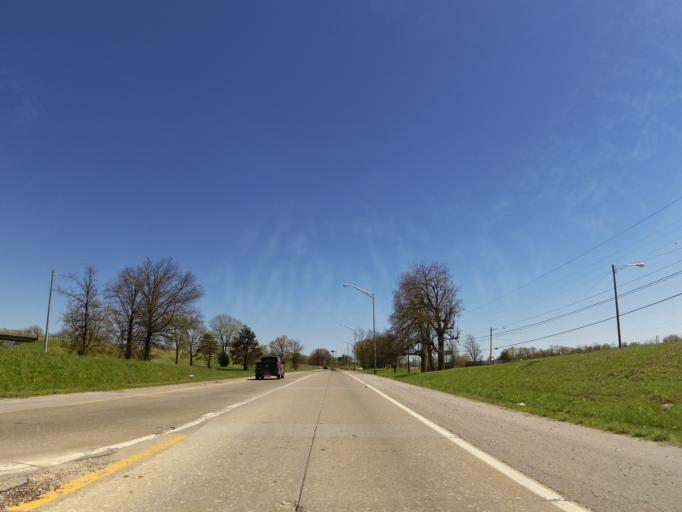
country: US
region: Kentucky
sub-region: Warren County
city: Bowling Green
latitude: 37.0099
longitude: -86.3832
